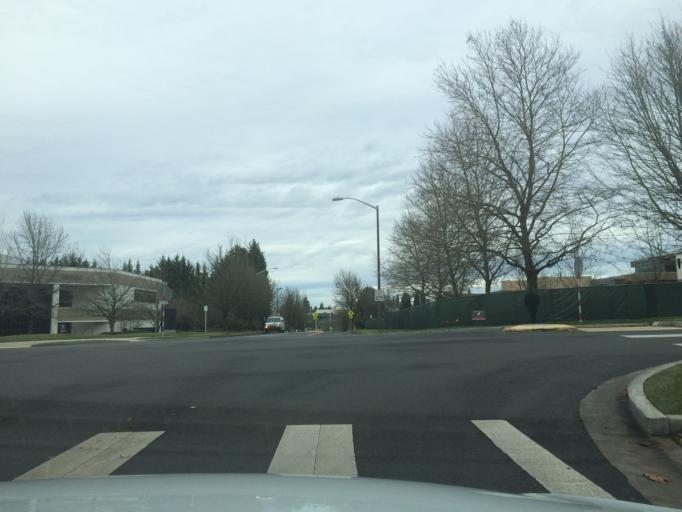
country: US
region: Washington
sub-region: King County
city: Redmond
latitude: 47.6423
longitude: -122.1306
